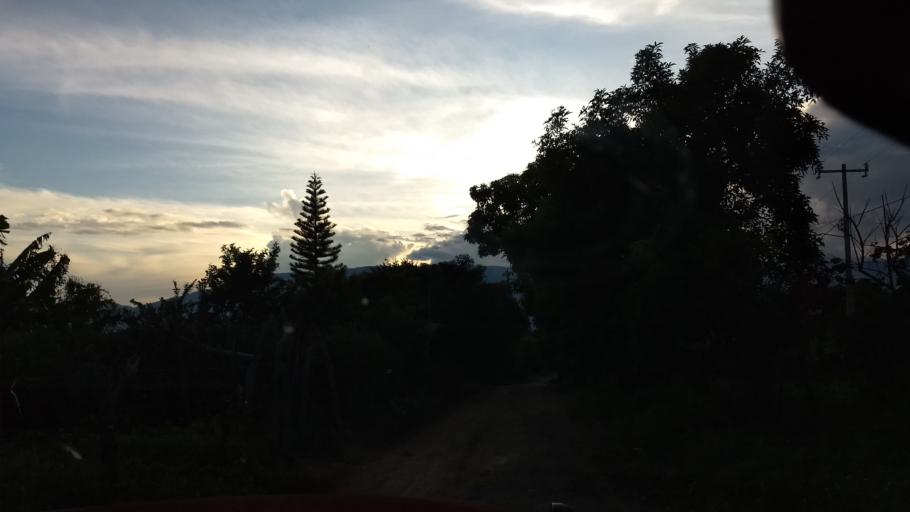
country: MX
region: Colima
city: Suchitlan
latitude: 19.4975
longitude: -103.7699
